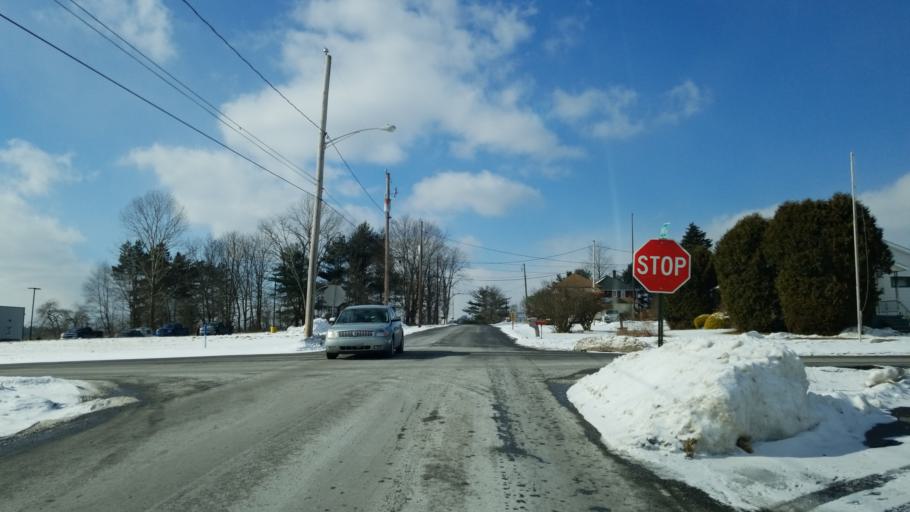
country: US
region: Pennsylvania
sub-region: Clearfield County
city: DuBois
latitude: 41.1246
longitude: -78.7332
